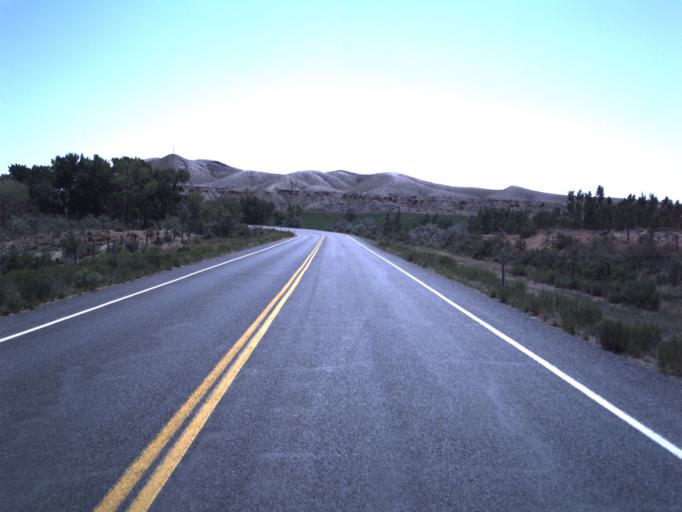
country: US
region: Utah
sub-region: Emery County
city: Orangeville
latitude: 39.2175
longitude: -111.0666
